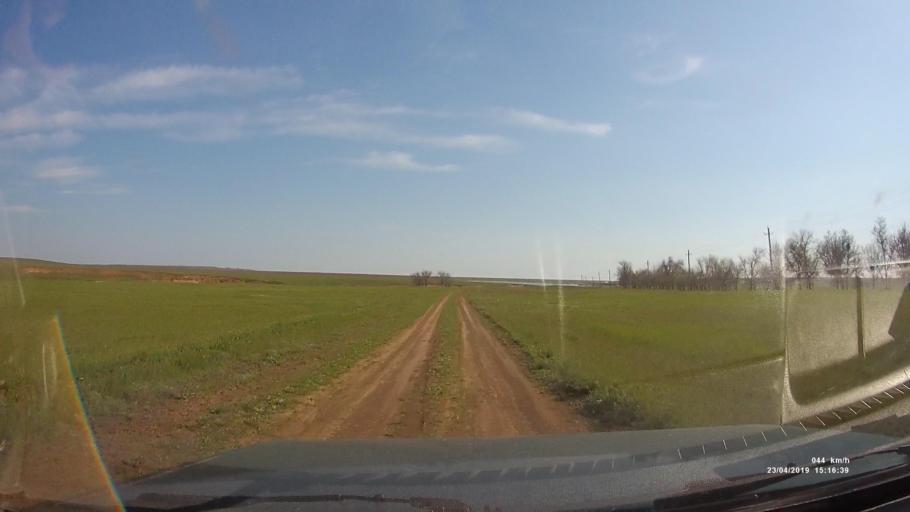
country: RU
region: Rostov
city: Remontnoye
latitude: 46.5325
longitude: 42.9694
